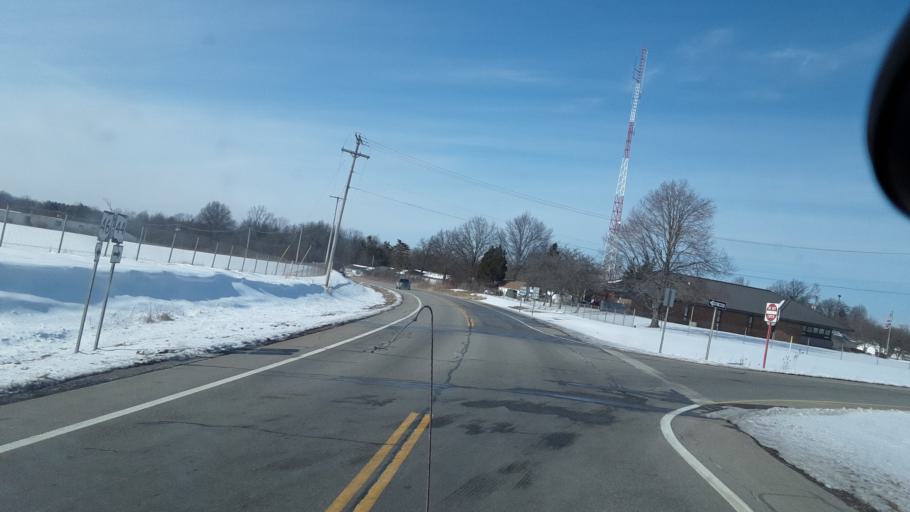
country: US
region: Ohio
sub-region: Mahoning County
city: Canfield
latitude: 41.0129
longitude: -80.7608
